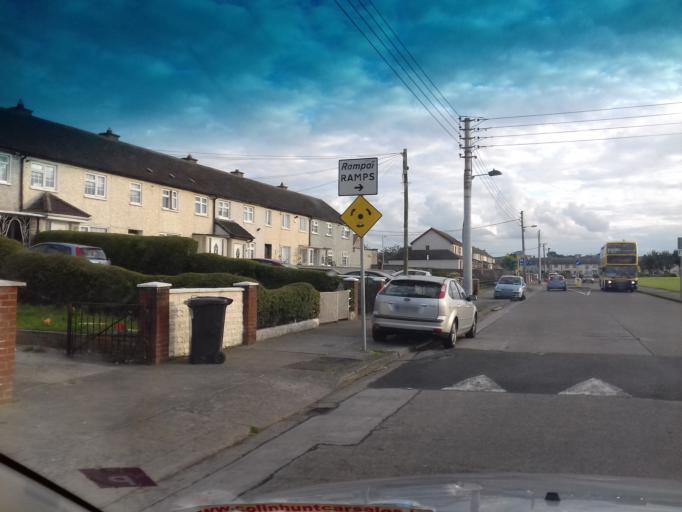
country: IE
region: Leinster
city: Artane
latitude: 53.3952
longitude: -6.2253
